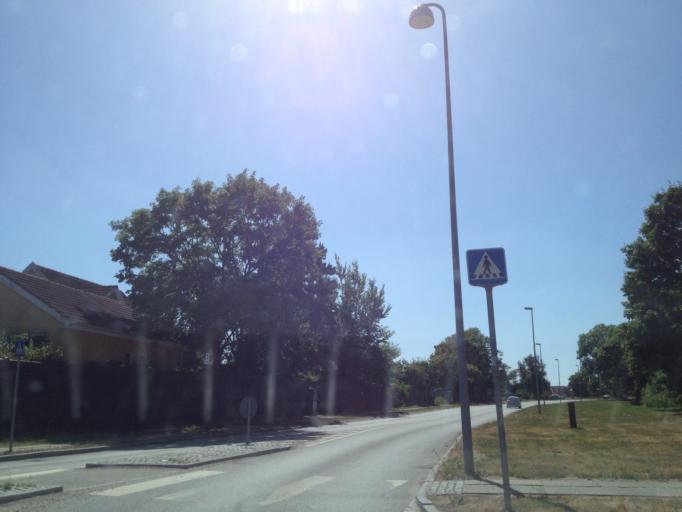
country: DK
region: Capital Region
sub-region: Fredensborg Kommune
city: Niva
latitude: 55.9366
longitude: 12.4952
